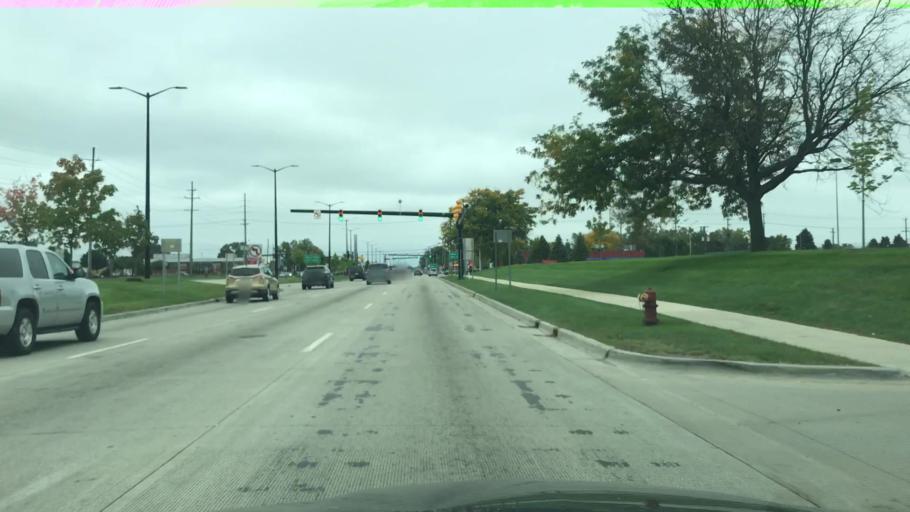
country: US
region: Michigan
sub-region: Macomb County
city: Sterling Heights
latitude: 42.5681
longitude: -83.0300
